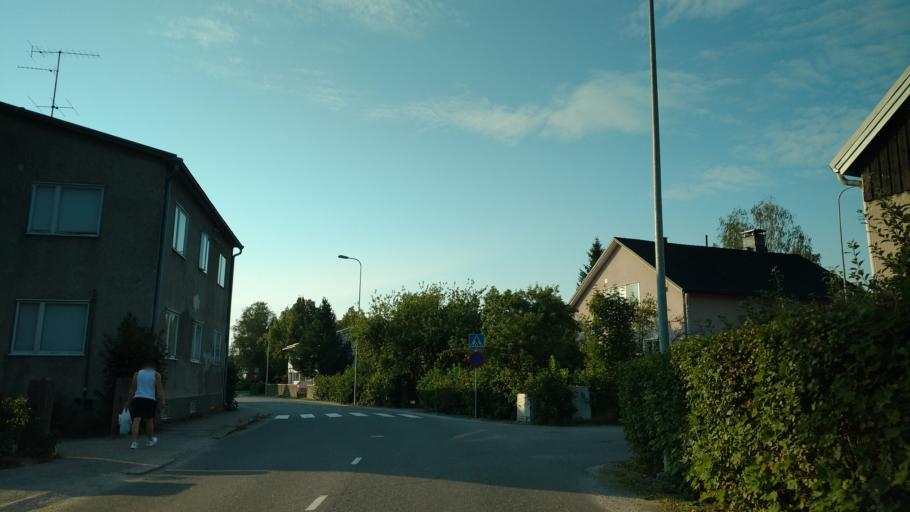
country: FI
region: Varsinais-Suomi
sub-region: Salo
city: Salo
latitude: 60.3879
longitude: 23.1426
